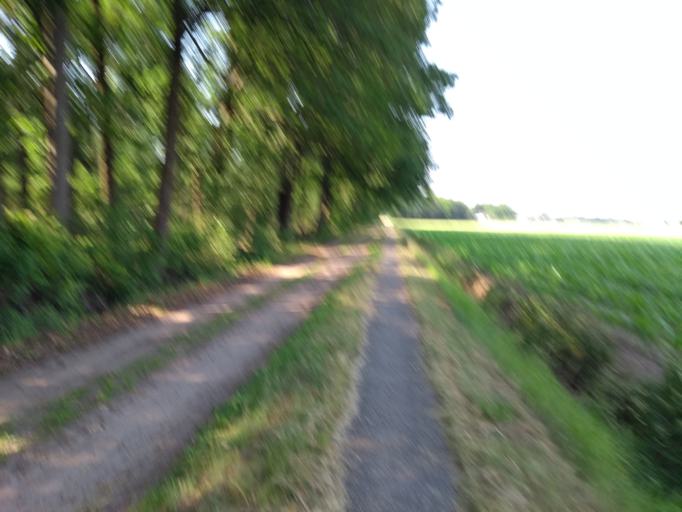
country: NL
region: Overijssel
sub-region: Gemeente Borne
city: Borne
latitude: 52.3528
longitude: 6.7271
